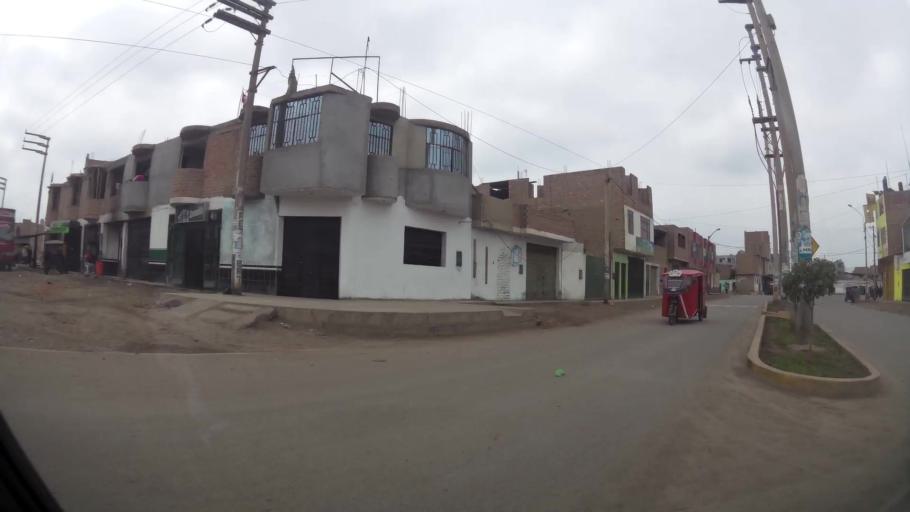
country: PE
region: Lima
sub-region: Provincia de Huaral
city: Huaral
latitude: -11.4974
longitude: -77.1989
